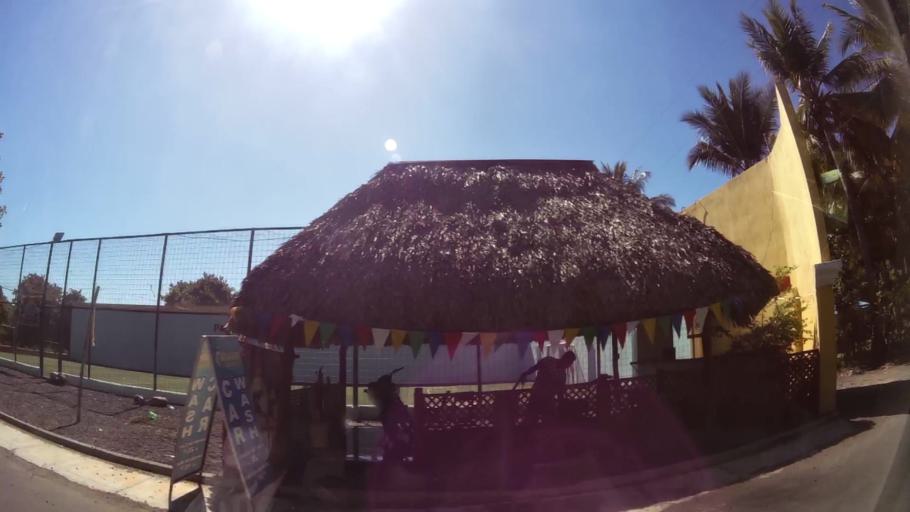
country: GT
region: Escuintla
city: Iztapa
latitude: 13.9323
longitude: -90.7026
